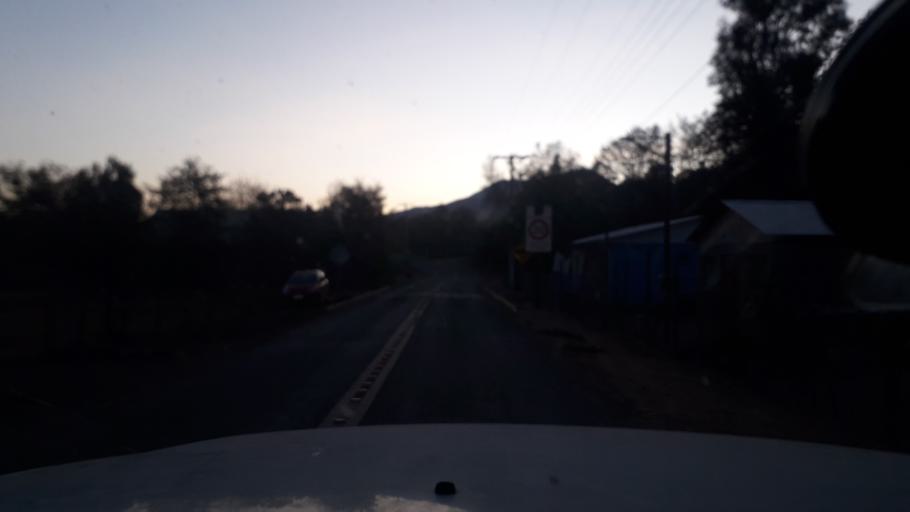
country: CL
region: Valparaiso
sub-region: Provincia de Marga Marga
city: Limache
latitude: -33.1684
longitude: -71.1433
